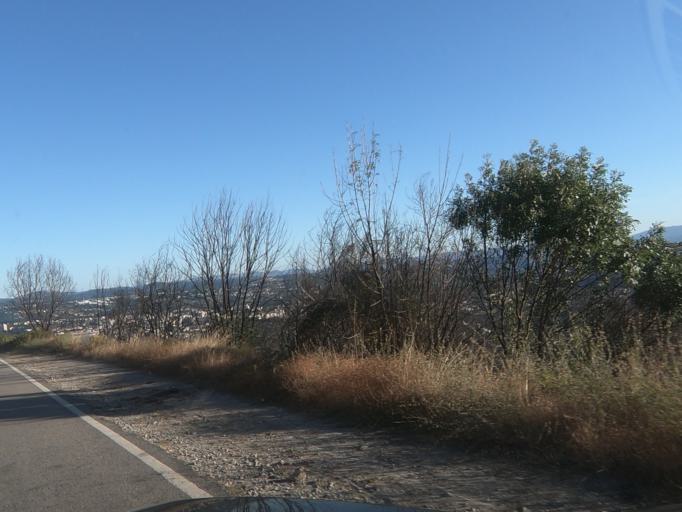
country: PT
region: Vila Real
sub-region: Vila Real
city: Vila Real
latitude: 41.3282
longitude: -7.7655
